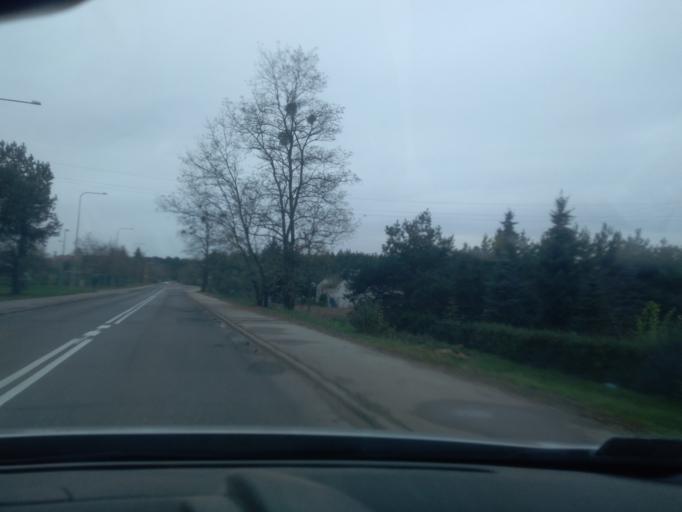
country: PL
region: Greater Poland Voivodeship
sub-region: Powiat poznanski
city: Murowana Goslina
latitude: 52.5449
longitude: 16.9727
